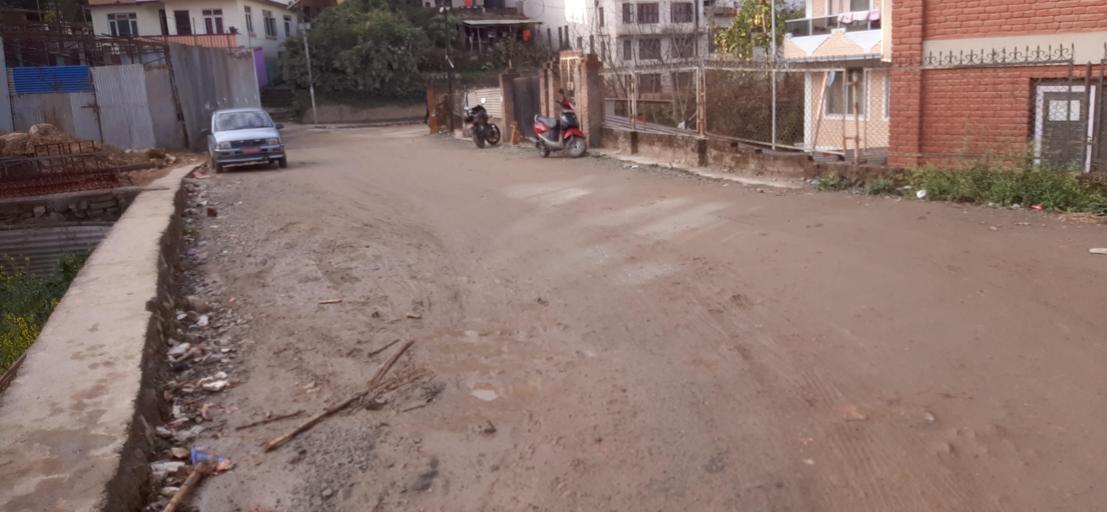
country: NP
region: Central Region
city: Kirtipur
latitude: 27.6745
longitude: 85.2820
